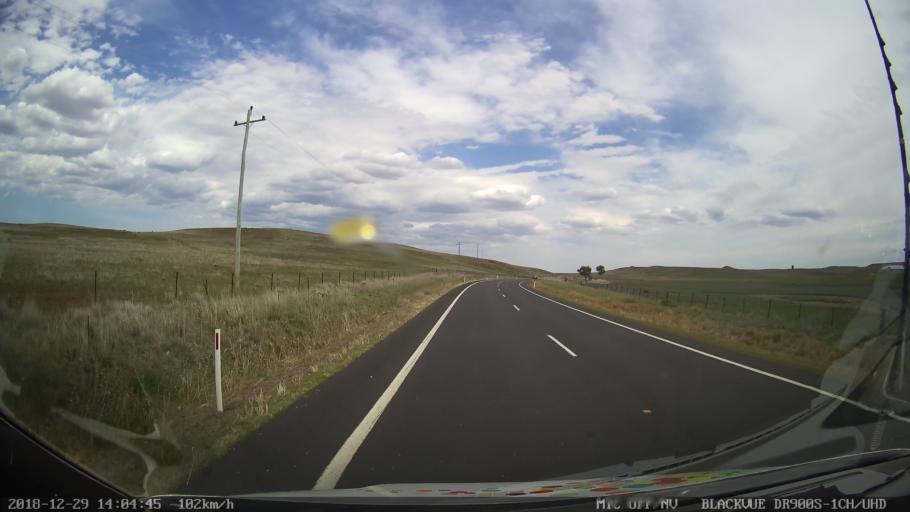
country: AU
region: New South Wales
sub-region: Cooma-Monaro
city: Cooma
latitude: -36.3206
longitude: 149.1885
